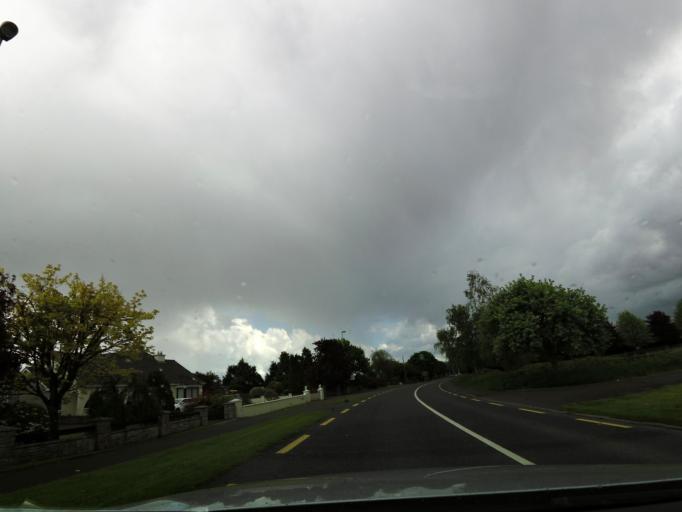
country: IE
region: Munster
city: Thurles
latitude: 52.6922
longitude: -7.8113
